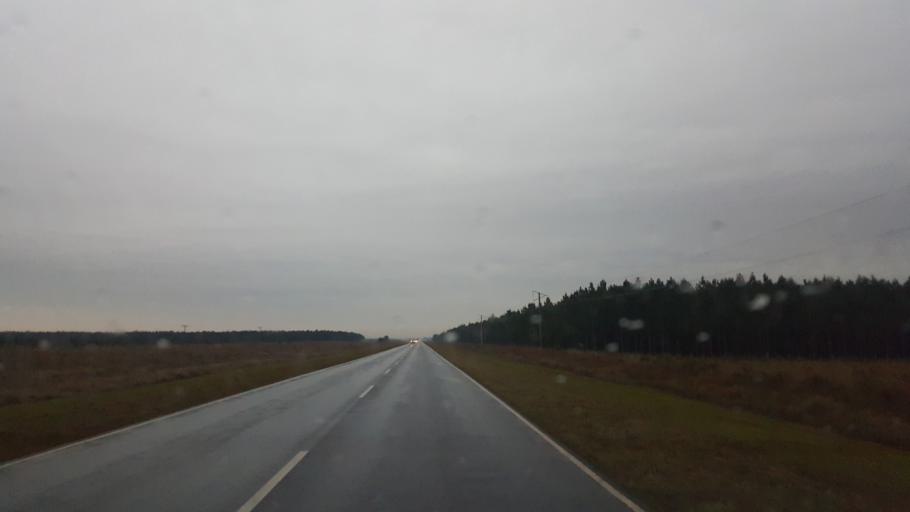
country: PY
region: Itapua
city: San Cosme y Damian
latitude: -27.5643
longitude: -56.2565
